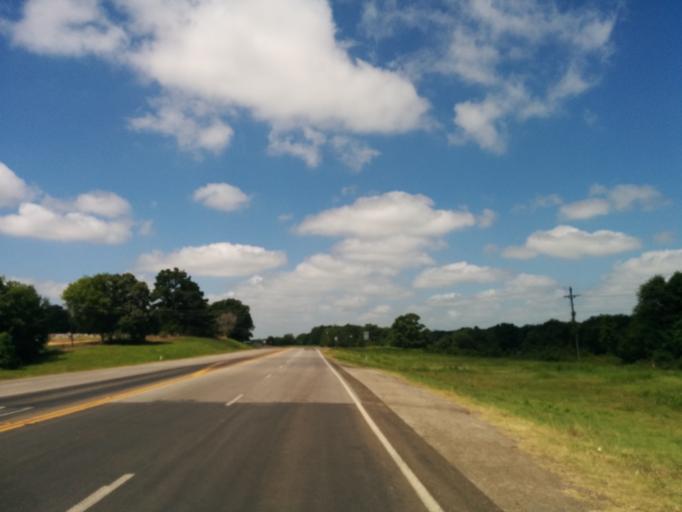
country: US
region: Texas
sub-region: Houston County
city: Crockett
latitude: 31.3357
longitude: -95.4666
